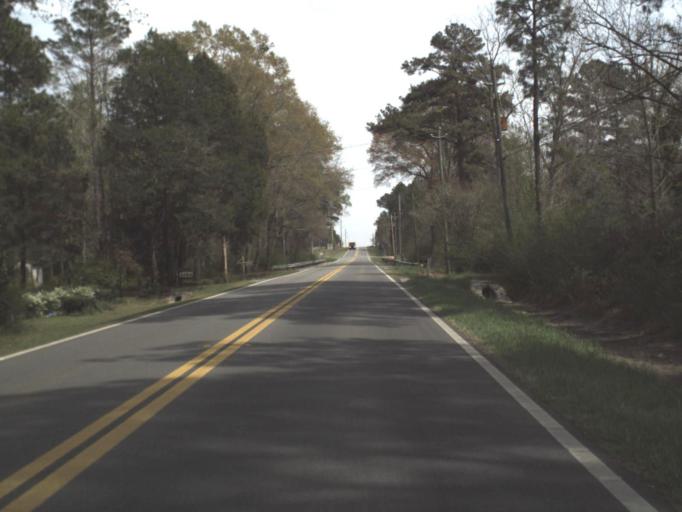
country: US
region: Florida
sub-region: Jackson County
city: Graceville
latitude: 30.9552
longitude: -85.4789
